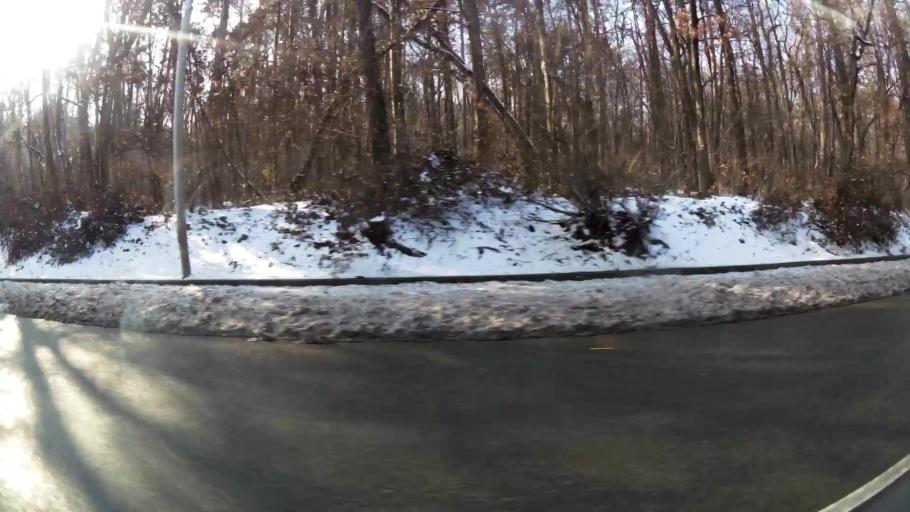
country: BG
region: Sofia-Capital
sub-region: Stolichna Obshtina
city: Sofia
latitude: 42.6689
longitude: 23.3376
